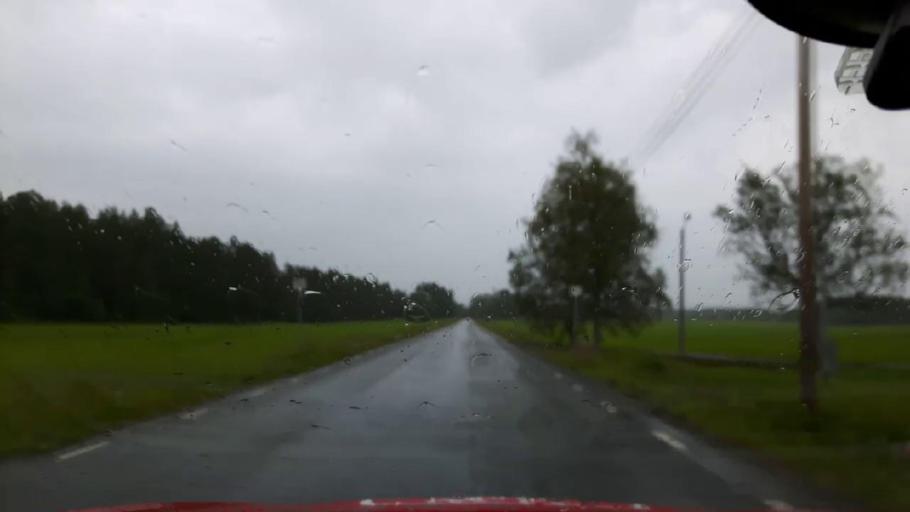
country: SE
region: Jaemtland
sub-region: OEstersunds Kommun
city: Brunflo
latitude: 62.9970
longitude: 14.7699
